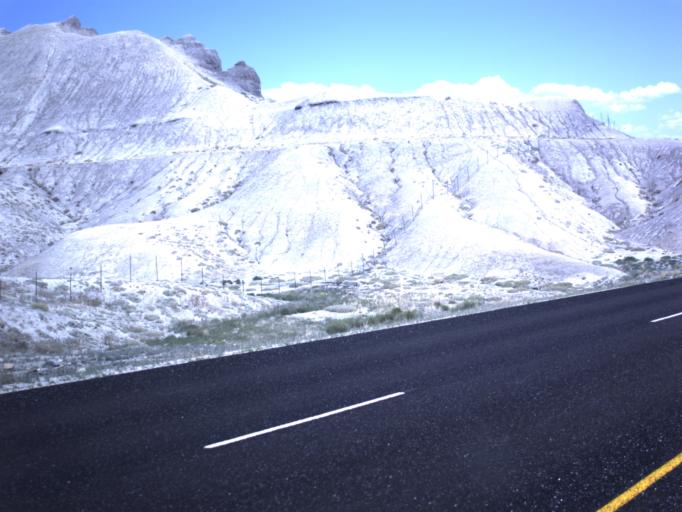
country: US
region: Utah
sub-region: Emery County
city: Ferron
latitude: 39.0392
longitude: -111.1266
